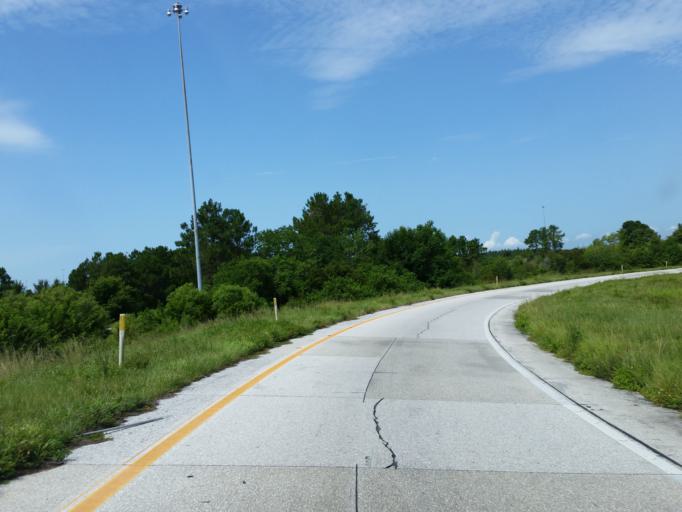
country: US
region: Florida
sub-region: Hillsborough County
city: Progress Village
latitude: 27.9251
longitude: -82.3292
